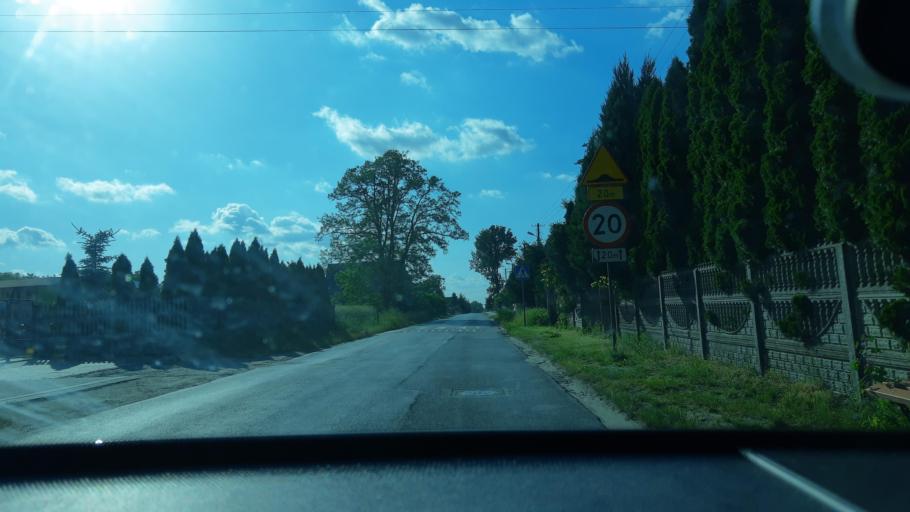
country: PL
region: Lodz Voivodeship
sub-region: Powiat sieradzki
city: Sieradz
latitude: 51.5465
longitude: 18.7807
